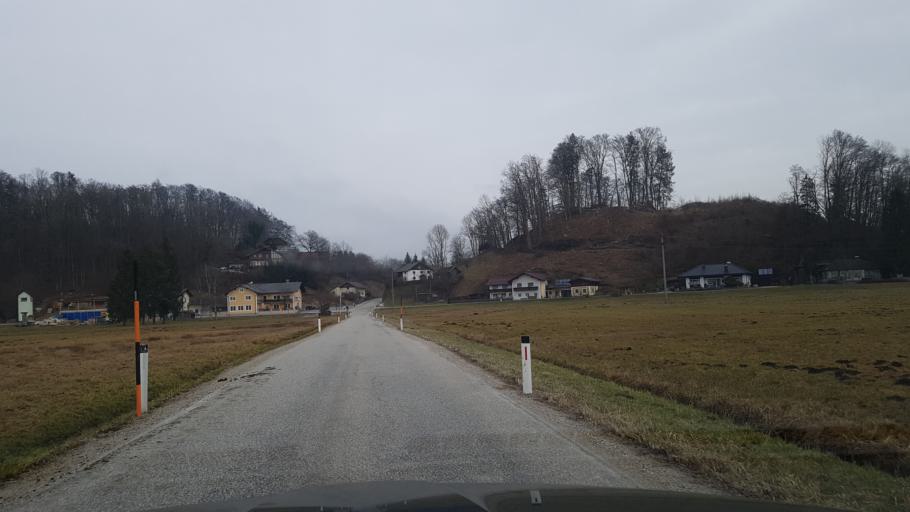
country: AT
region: Salzburg
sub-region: Politischer Bezirk Salzburg-Umgebung
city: Dorfbeuern
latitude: 48.0624
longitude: 12.9611
